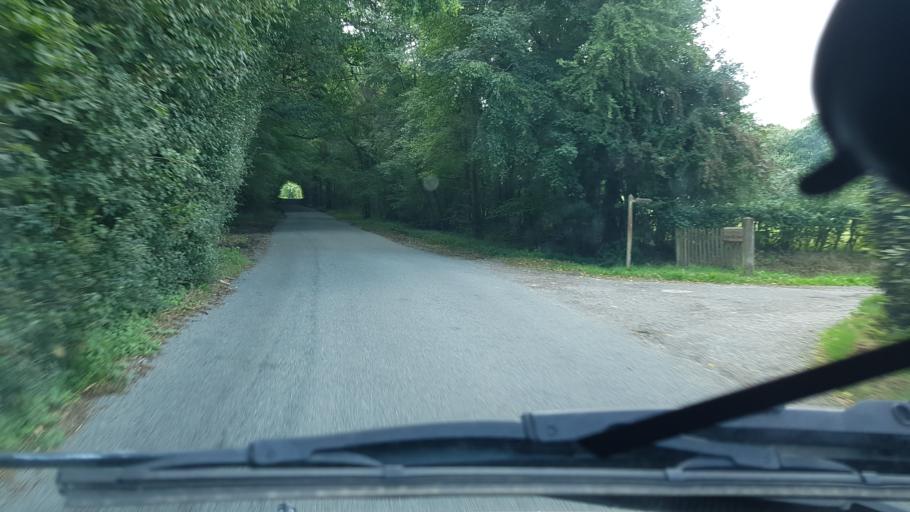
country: GB
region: England
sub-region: Surrey
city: Ockley
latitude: 51.1029
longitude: -0.3635
